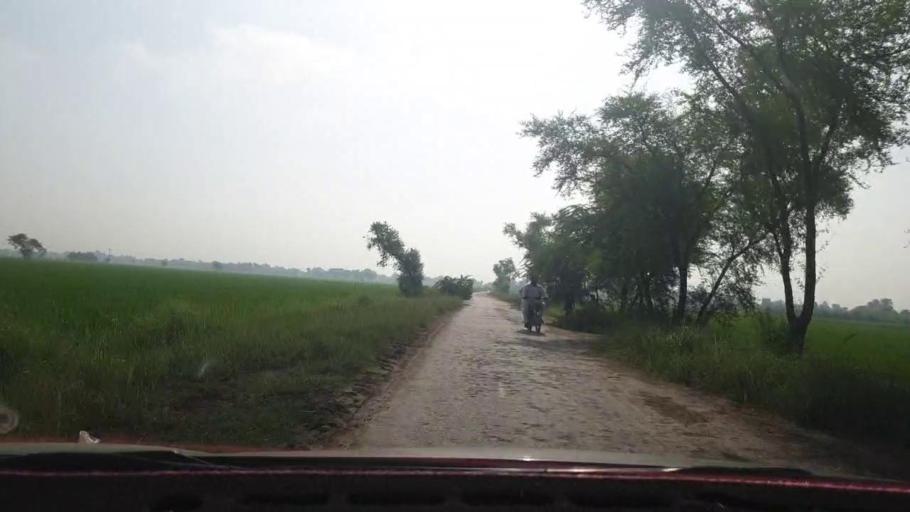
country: PK
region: Sindh
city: Nasirabad
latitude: 27.4559
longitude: 67.9562
